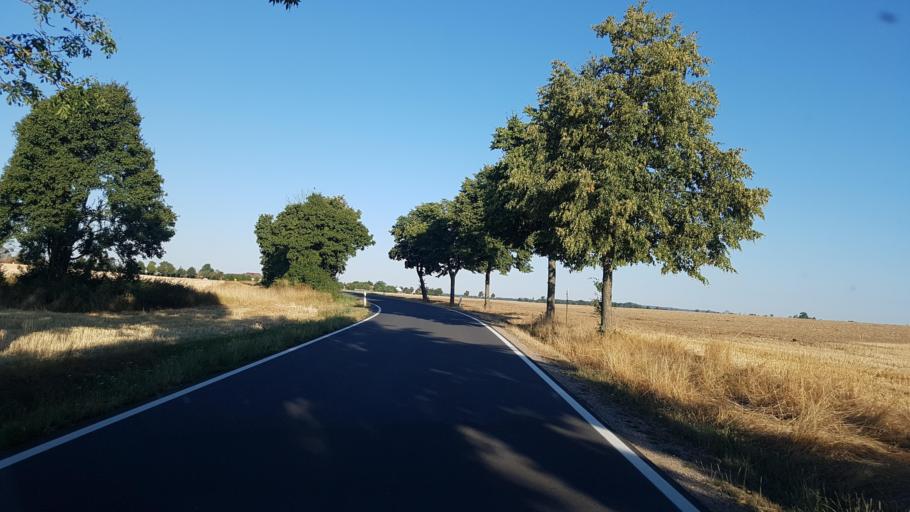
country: DE
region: Saxony
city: Dahlen
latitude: 51.3654
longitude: 12.9638
